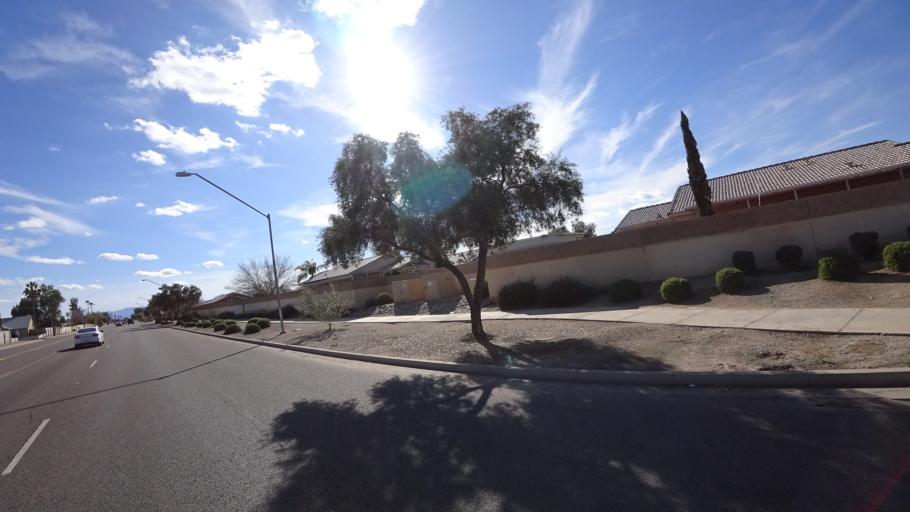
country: US
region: Arizona
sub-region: Maricopa County
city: Glendale
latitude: 33.5140
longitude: -112.2206
